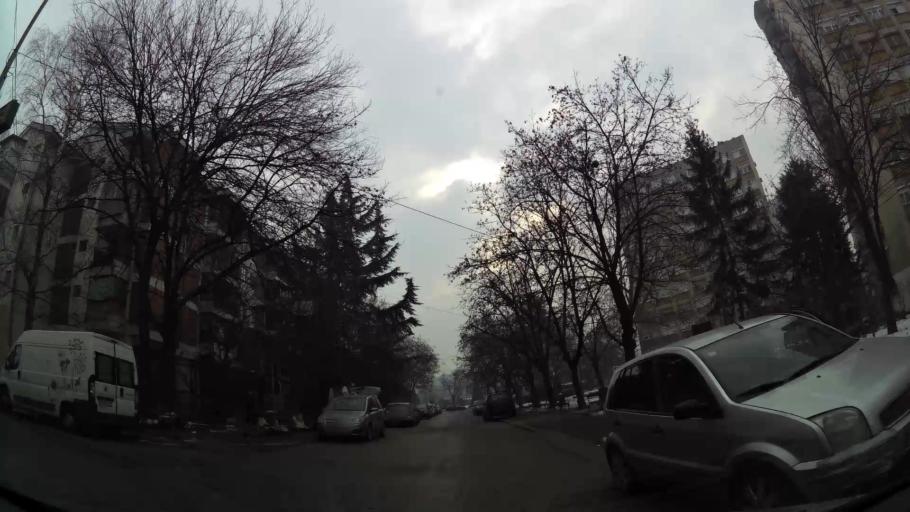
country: MK
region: Cair
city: Cair
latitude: 42.0029
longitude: 21.4621
